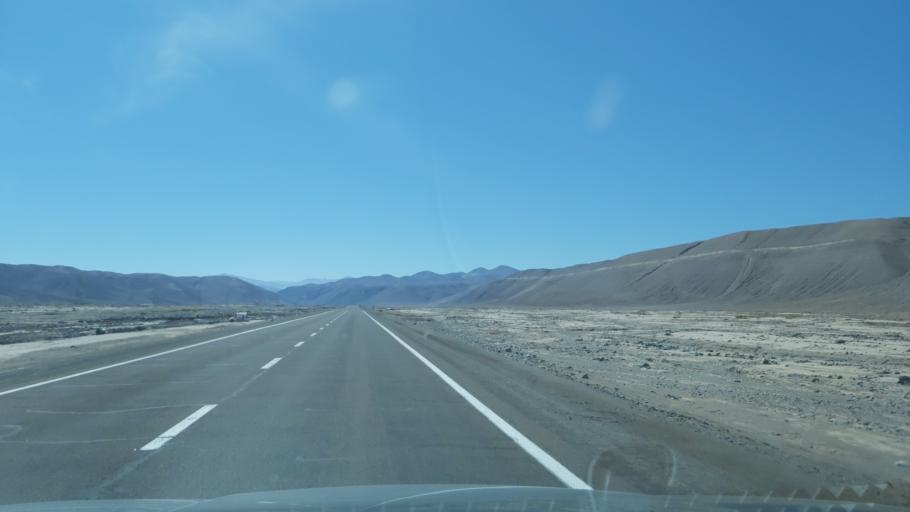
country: CL
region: Atacama
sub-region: Provincia de Chanaral
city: Diego de Almagro
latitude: -26.3530
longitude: -69.9041
